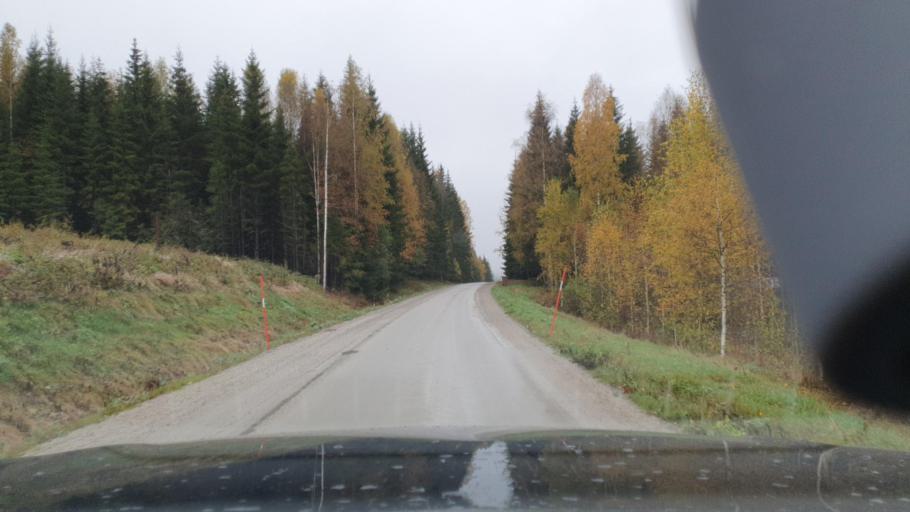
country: SE
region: Vaermland
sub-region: Arvika Kommun
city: Arvika
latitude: 59.7956
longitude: 12.7511
